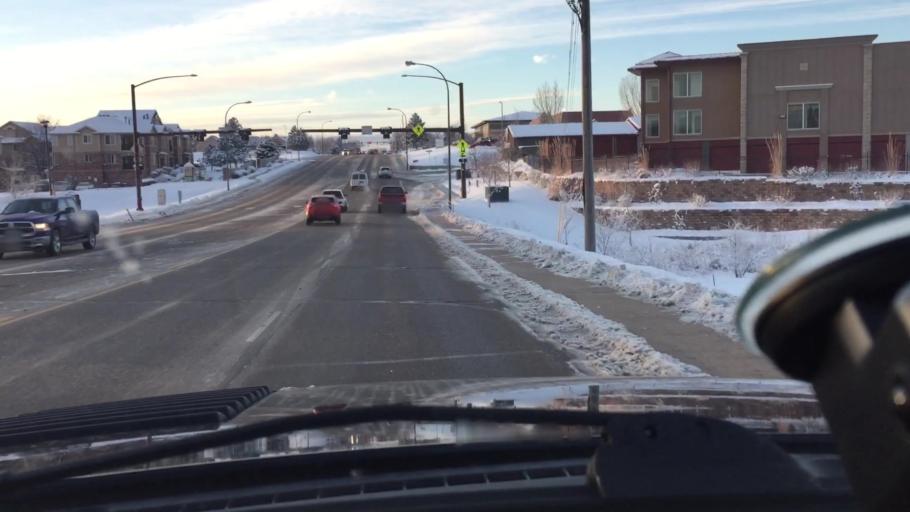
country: US
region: Colorado
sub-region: Adams County
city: Federal Heights
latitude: 39.8608
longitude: -104.9967
